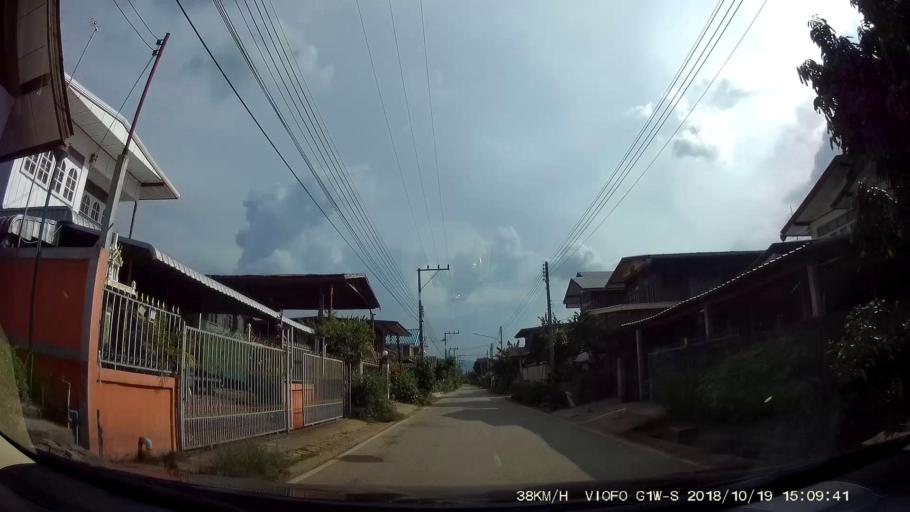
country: TH
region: Chaiyaphum
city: Phu Khiao
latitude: 16.4092
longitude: 102.1033
